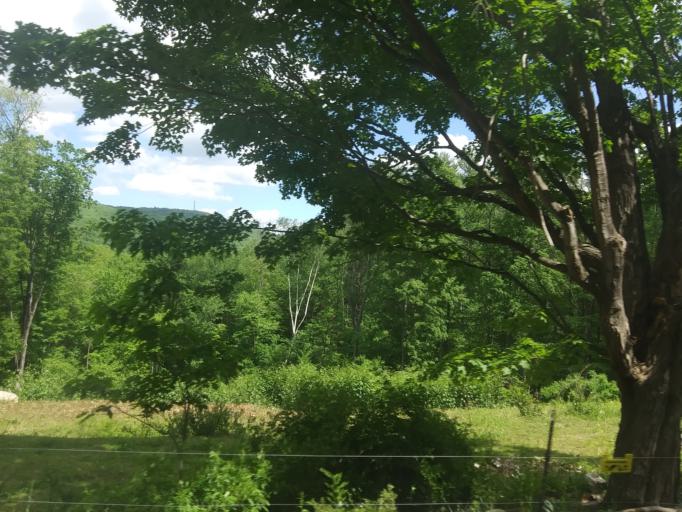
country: US
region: Massachusetts
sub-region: Franklin County
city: Shelburne Falls
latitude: 42.5964
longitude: -72.7446
